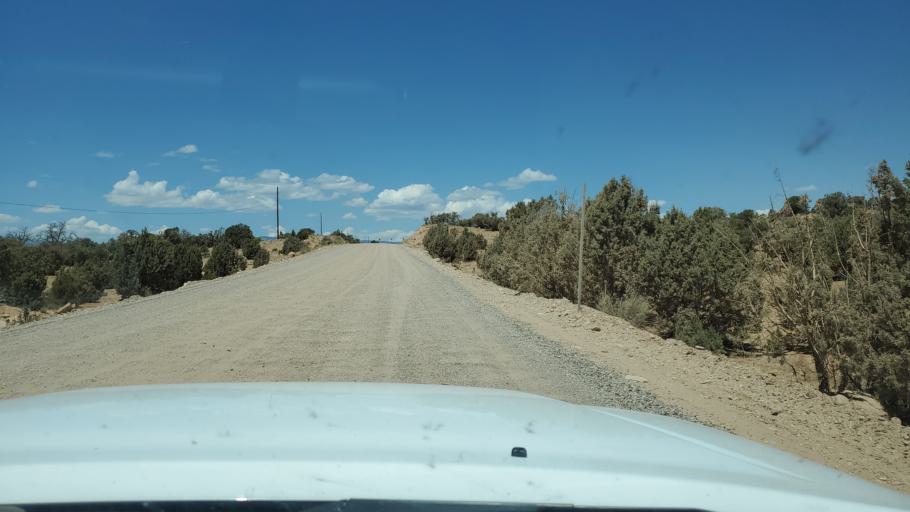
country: US
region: Utah
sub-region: Wayne County
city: Loa
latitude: 37.7260
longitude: -111.5296
